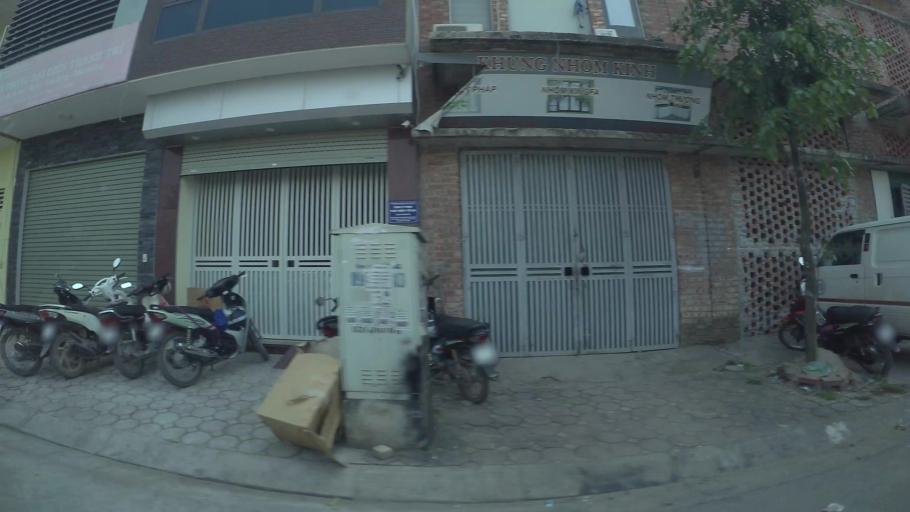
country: VN
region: Ha Noi
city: Ha Dong
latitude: 20.9667
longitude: 105.7997
